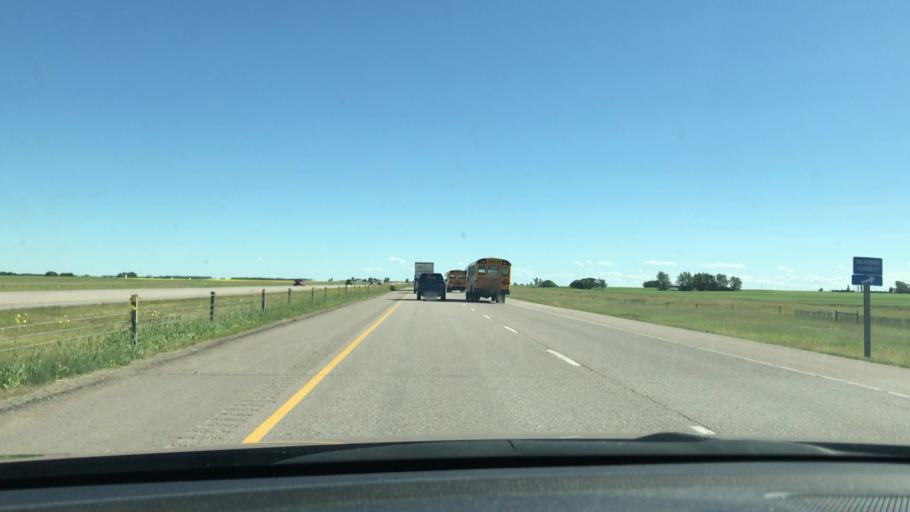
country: CA
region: Alberta
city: Didsbury
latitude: 51.6947
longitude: -114.0256
